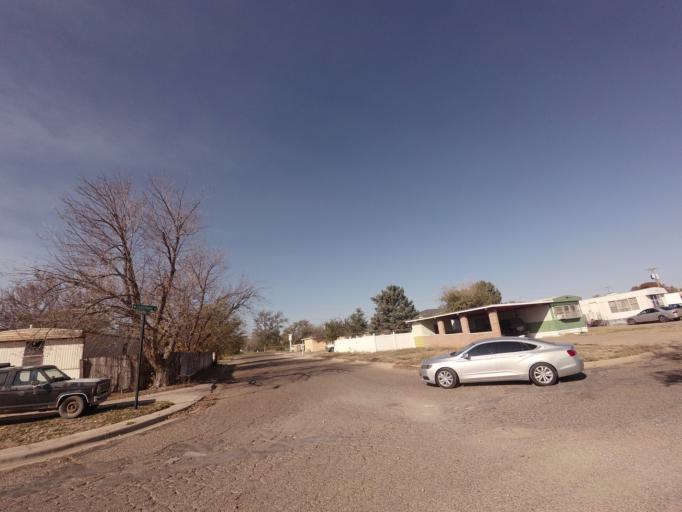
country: US
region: New Mexico
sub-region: Curry County
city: Clovis
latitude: 34.4095
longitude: -103.1778
